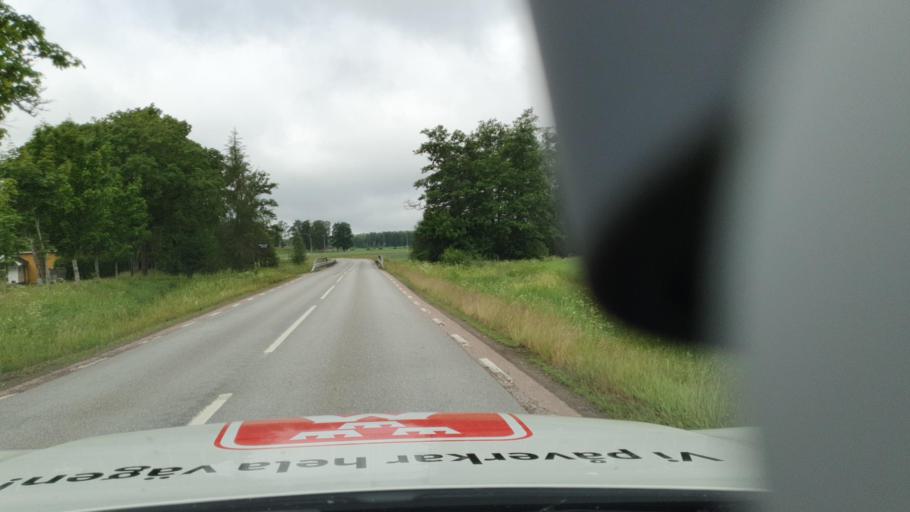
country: SE
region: Vaermland
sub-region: Kristinehamns Kommun
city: Bjorneborg
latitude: 59.1173
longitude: 14.1819
